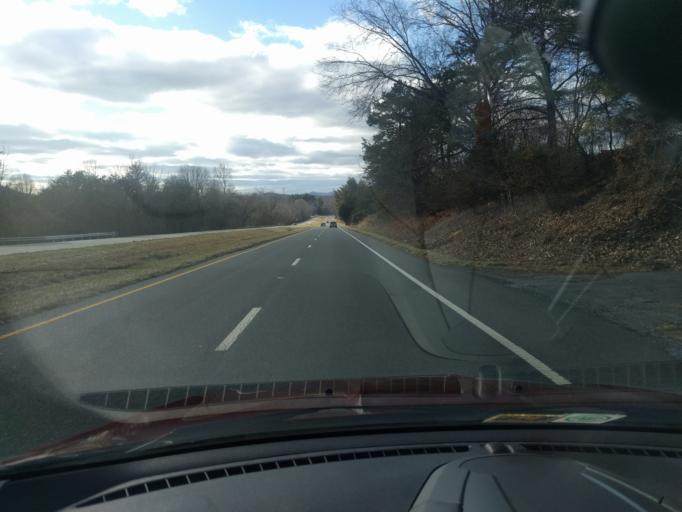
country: US
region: Virginia
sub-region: City of Bedford
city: Bedford
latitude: 37.3518
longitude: -79.6084
